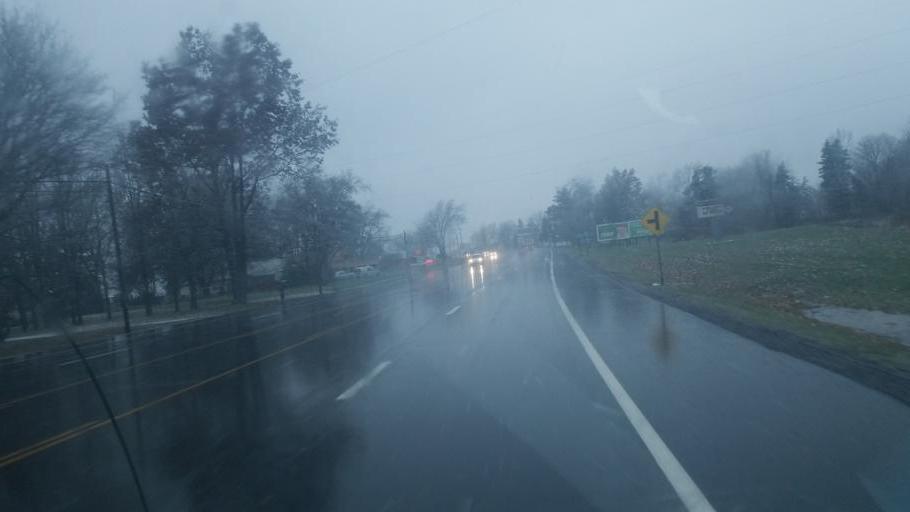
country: US
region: Ohio
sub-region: Richland County
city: Shelby
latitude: 40.8537
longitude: -82.6276
